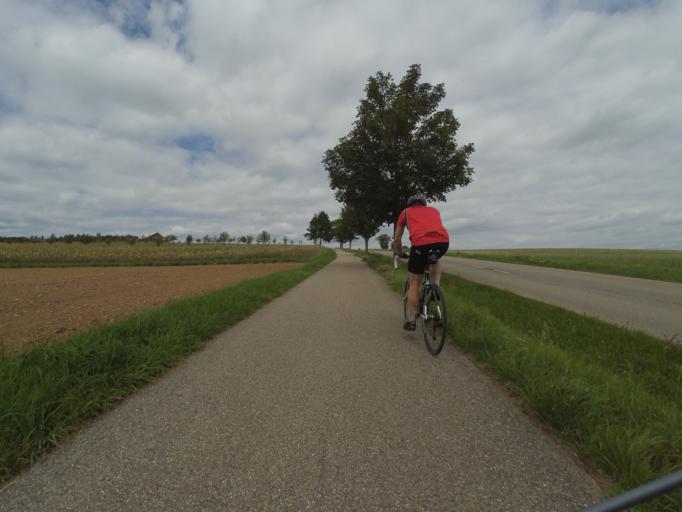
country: DE
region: Baden-Wuerttemberg
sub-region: Freiburg Region
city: Loffingen
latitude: 47.8591
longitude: 8.3486
